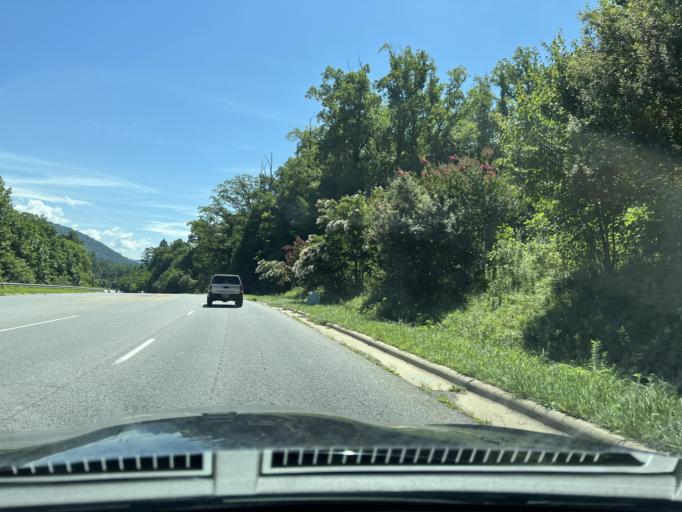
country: US
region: North Carolina
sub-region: Buncombe County
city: Fairview
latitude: 35.5458
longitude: -82.4529
